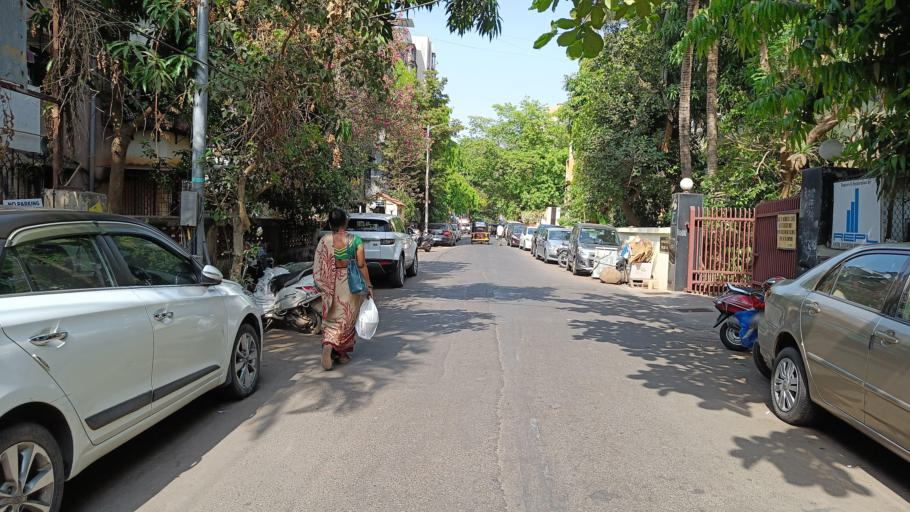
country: IN
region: Maharashtra
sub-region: Mumbai Suburban
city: Powai
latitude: 19.1425
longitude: 72.8236
